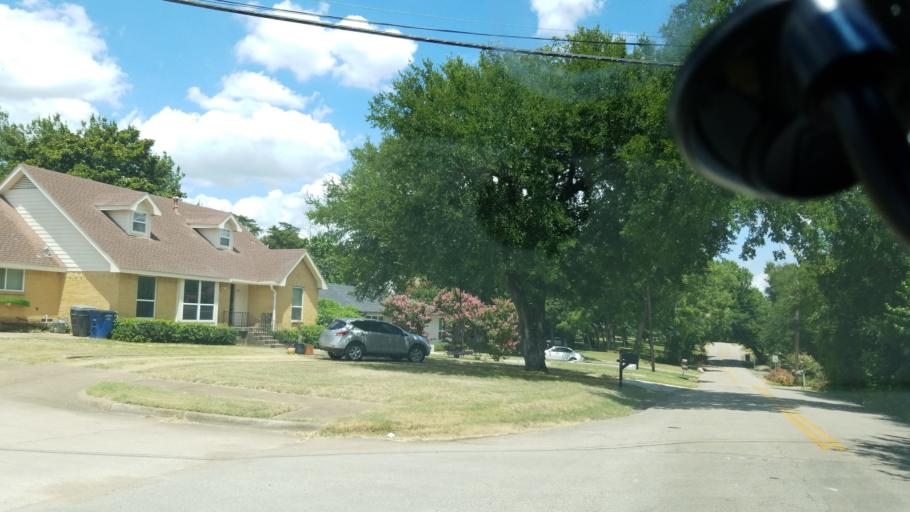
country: US
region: Texas
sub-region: Dallas County
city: Cockrell Hill
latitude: 32.6945
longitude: -96.8696
